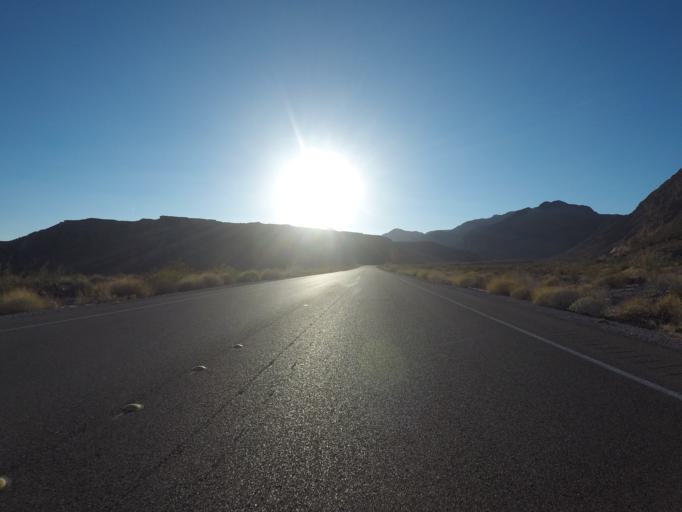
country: US
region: Nevada
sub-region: Clark County
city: Moapa Valley
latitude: 36.3638
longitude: -114.4668
